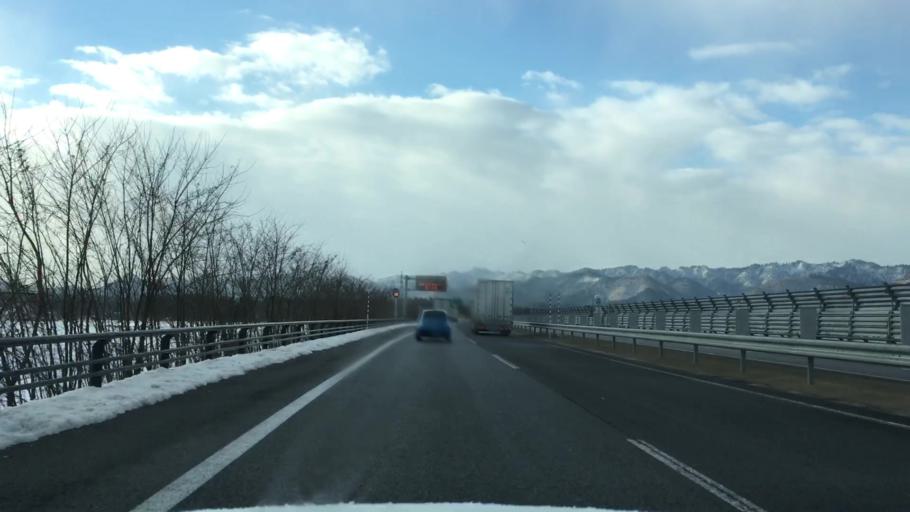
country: JP
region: Akita
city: Odate
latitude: 40.2560
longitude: 140.5205
